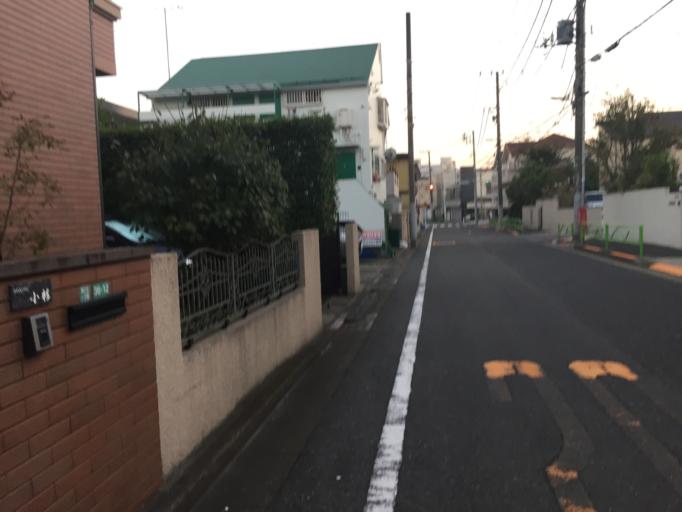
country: JP
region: Tokyo
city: Tokyo
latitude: 35.6316
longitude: 139.6646
